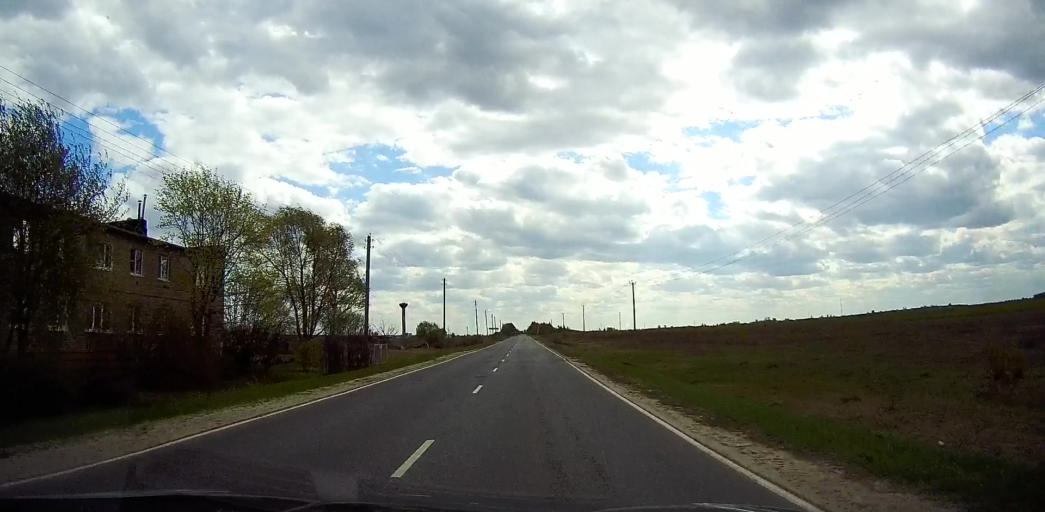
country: RU
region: Moskovskaya
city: Davydovo
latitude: 55.6432
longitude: 38.7500
